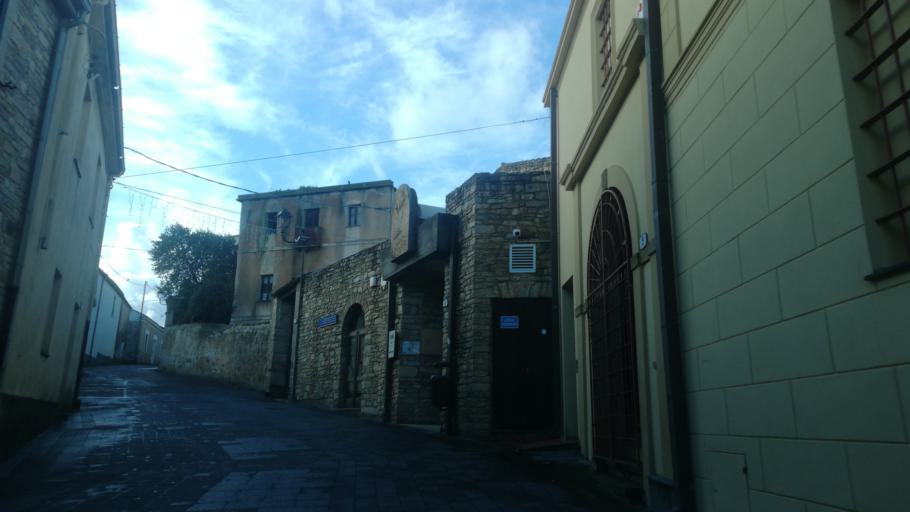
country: IT
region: Sardinia
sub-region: Provincia di Medio Campidano
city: Villanovaforru
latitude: 39.6327
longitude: 8.8683
